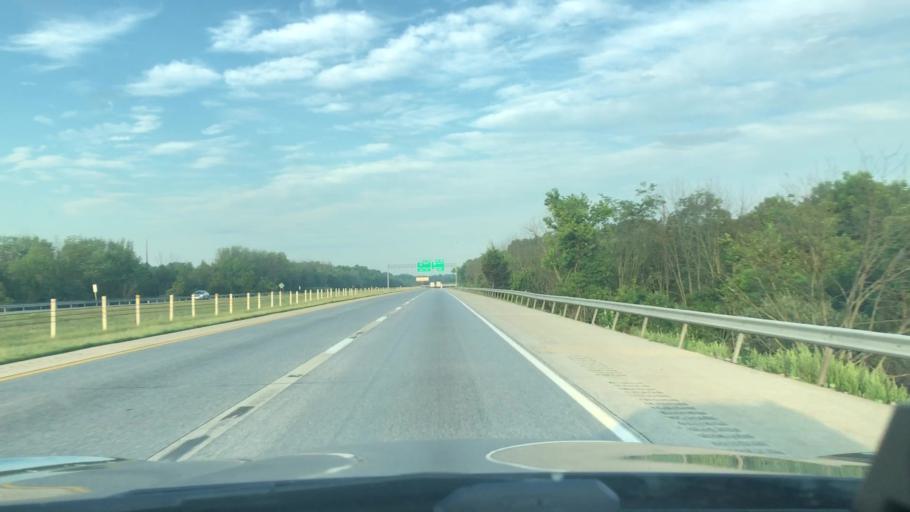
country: US
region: Pennsylvania
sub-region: Lebanon County
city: Jonestown
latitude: 40.4346
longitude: -76.4941
